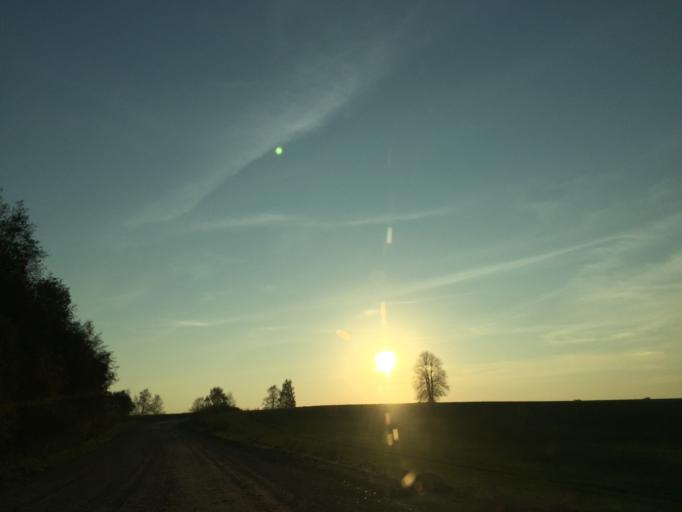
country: LV
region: Vainode
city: Vainode
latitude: 56.4871
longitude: 21.7655
